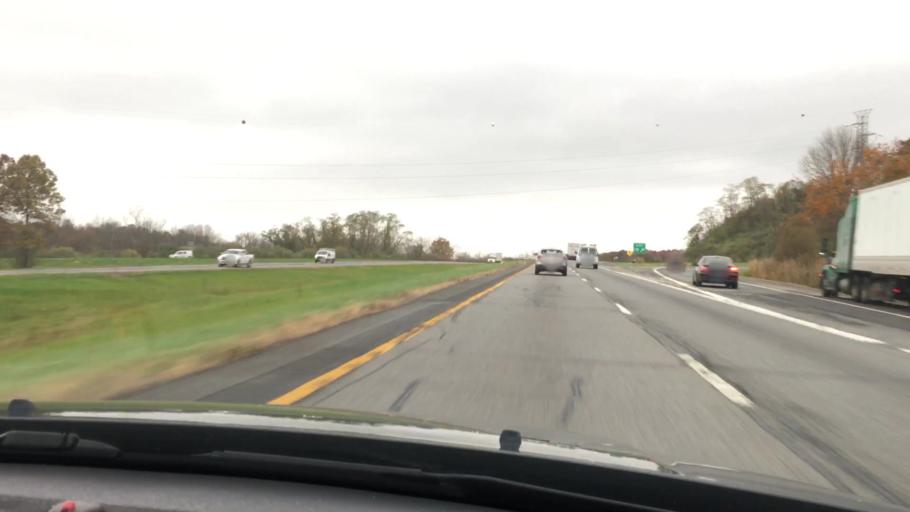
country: US
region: New York
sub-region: Putnam County
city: Brewster Hill
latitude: 41.4252
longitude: -73.6268
